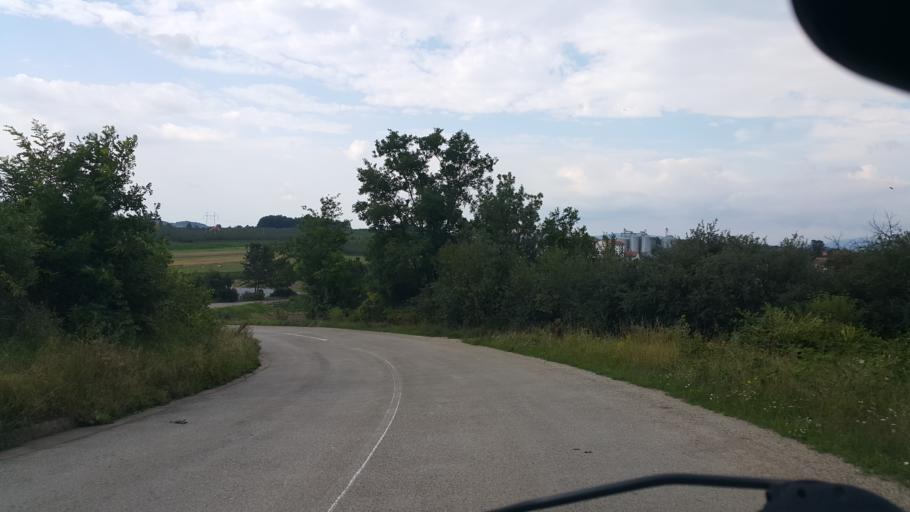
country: RS
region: Central Serbia
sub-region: Toplicki Okrug
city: Blace
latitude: 43.2569
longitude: 21.2680
